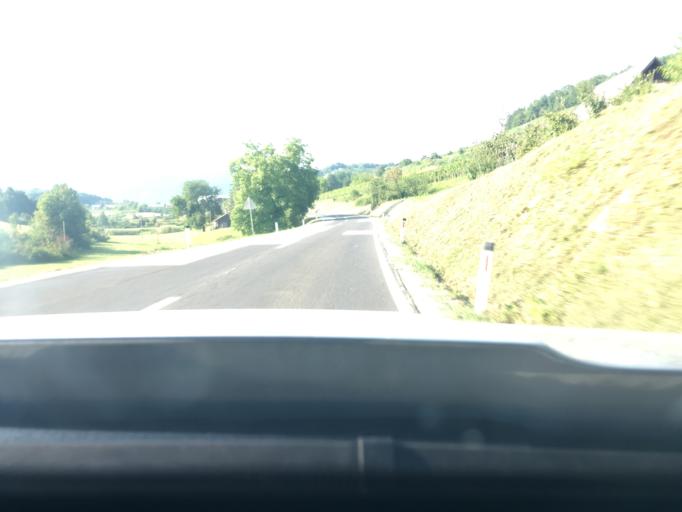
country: SI
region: Metlika
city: Metlika
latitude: 45.6734
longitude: 15.2854
